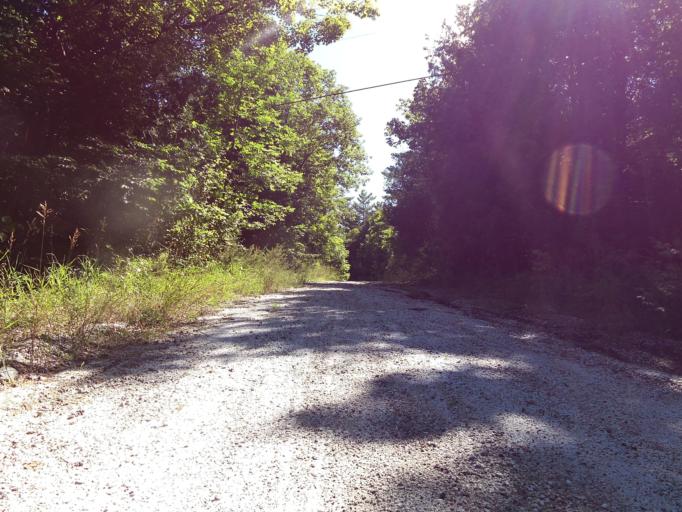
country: CA
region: Ontario
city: Arnprior
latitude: 45.1623
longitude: -76.4898
